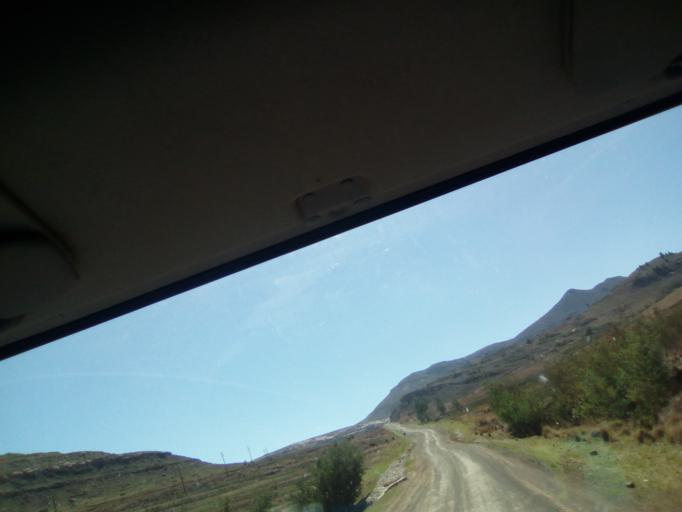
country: LS
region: Qacha's Nek
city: Qacha's Nek
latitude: -30.0447
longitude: 28.6448
